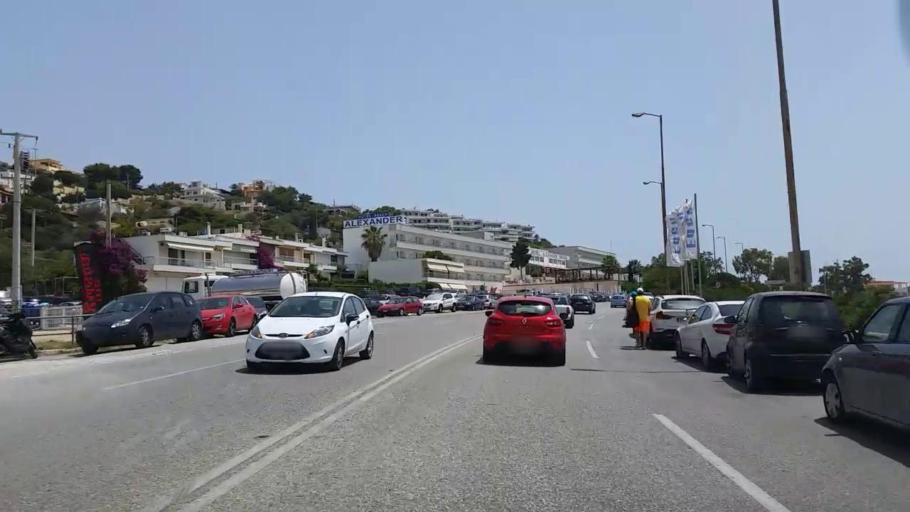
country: GR
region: Attica
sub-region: Nomarchia Anatolikis Attikis
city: Saronida
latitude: 37.7274
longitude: 23.9080
